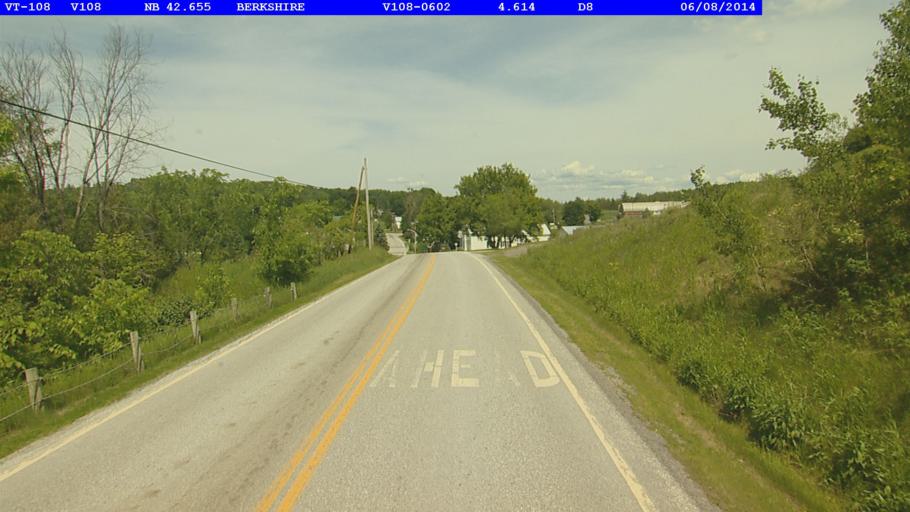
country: US
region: Vermont
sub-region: Franklin County
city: Enosburg Falls
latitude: 44.9873
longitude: -72.8154
